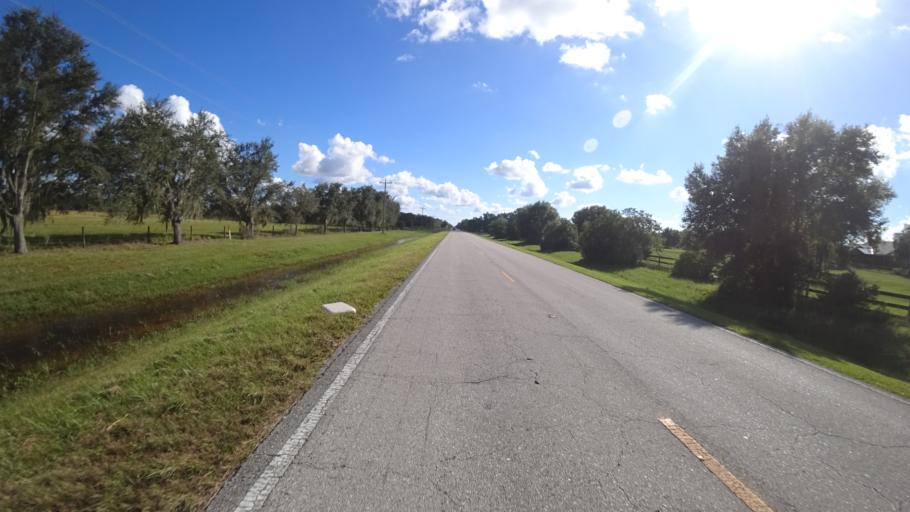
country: US
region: Florida
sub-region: Sarasota County
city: The Meadows
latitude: 27.4178
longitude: -82.3037
